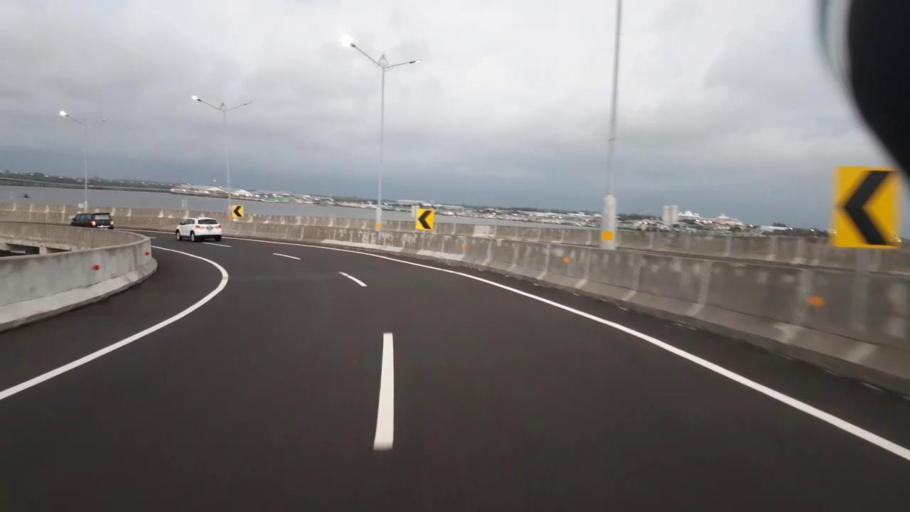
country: ID
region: Bali
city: Kelanabian
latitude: -8.7449
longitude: 115.1970
